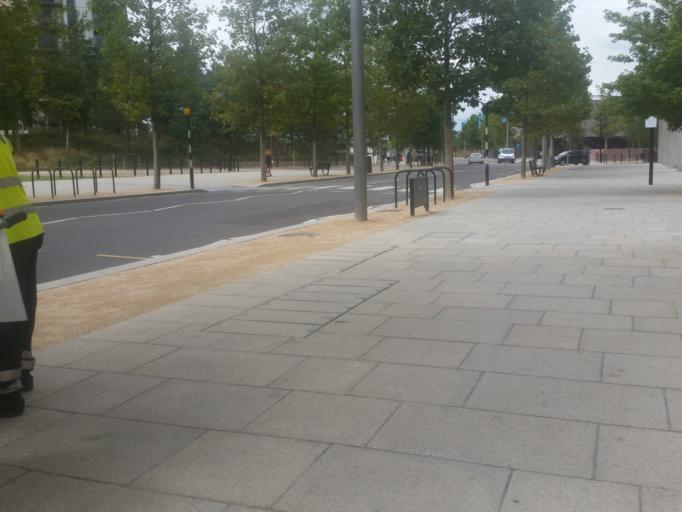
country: GB
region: England
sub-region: Greater London
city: Poplar
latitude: 51.5478
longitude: -0.0081
